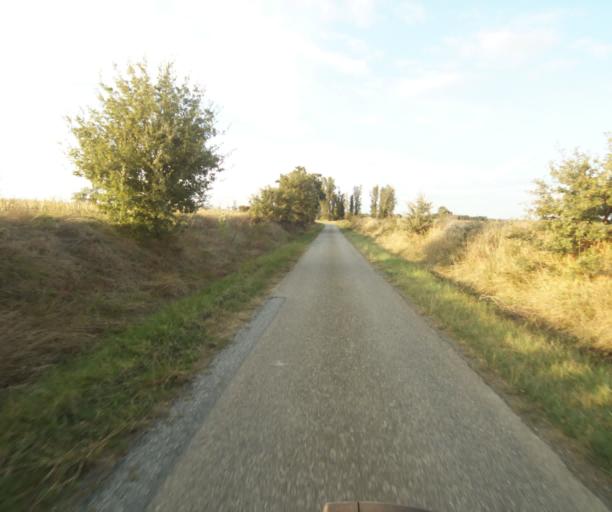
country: FR
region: Midi-Pyrenees
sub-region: Departement de la Haute-Garonne
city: Launac
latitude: 43.8110
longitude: 1.1637
